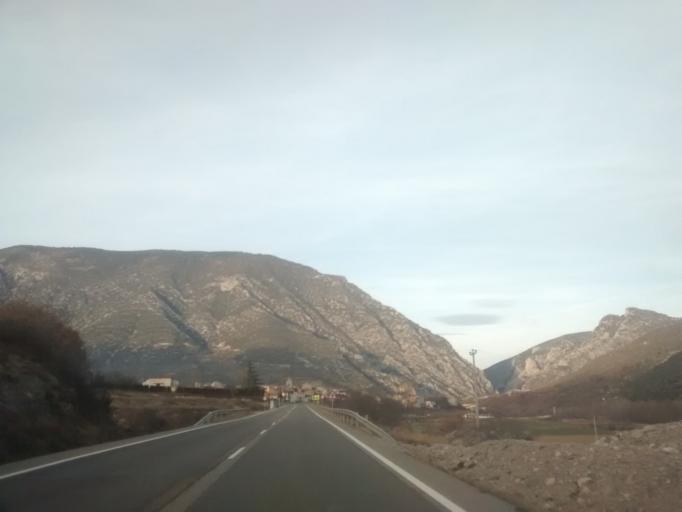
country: ES
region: Catalonia
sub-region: Provincia de Lleida
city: Coll de Nargo
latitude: 42.2030
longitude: 1.3276
